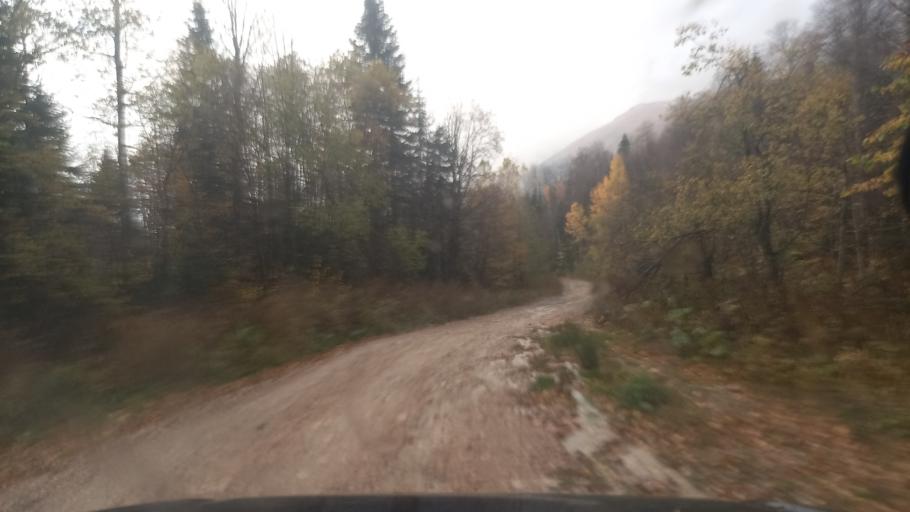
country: RU
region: Krasnodarskiy
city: Gornoye Loo
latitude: 44.0077
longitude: 39.8435
